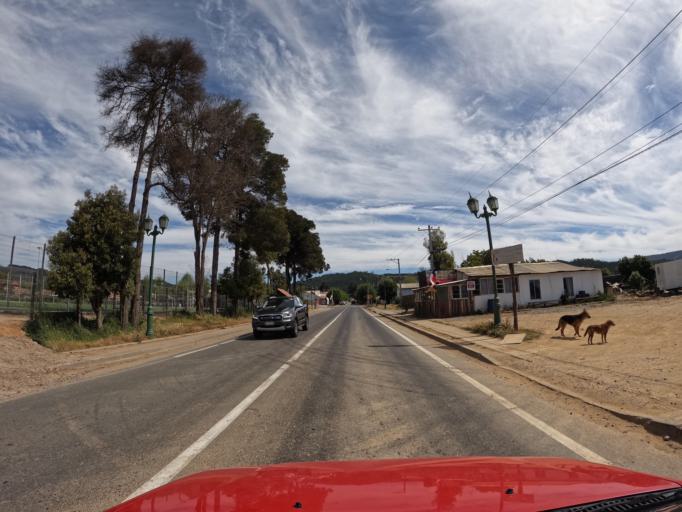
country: CL
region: Maule
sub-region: Provincia de Talca
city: Constitucion
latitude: -35.0884
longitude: -72.0204
